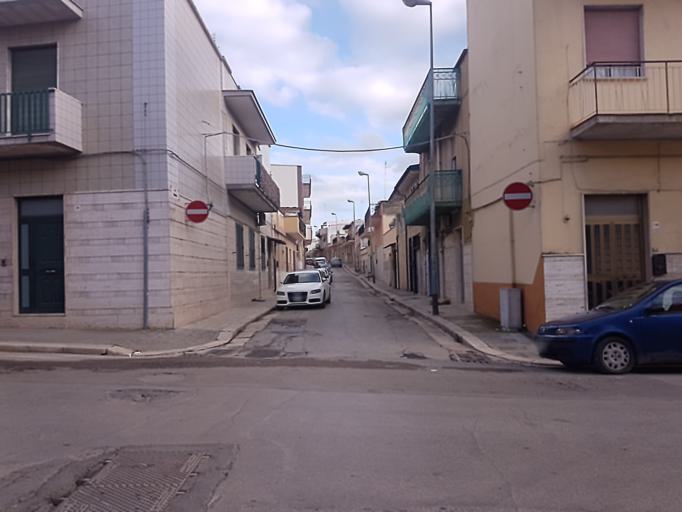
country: IT
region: Apulia
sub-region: Provincia di Barletta - Andria - Trani
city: Andria
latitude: 41.2297
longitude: 16.2859
